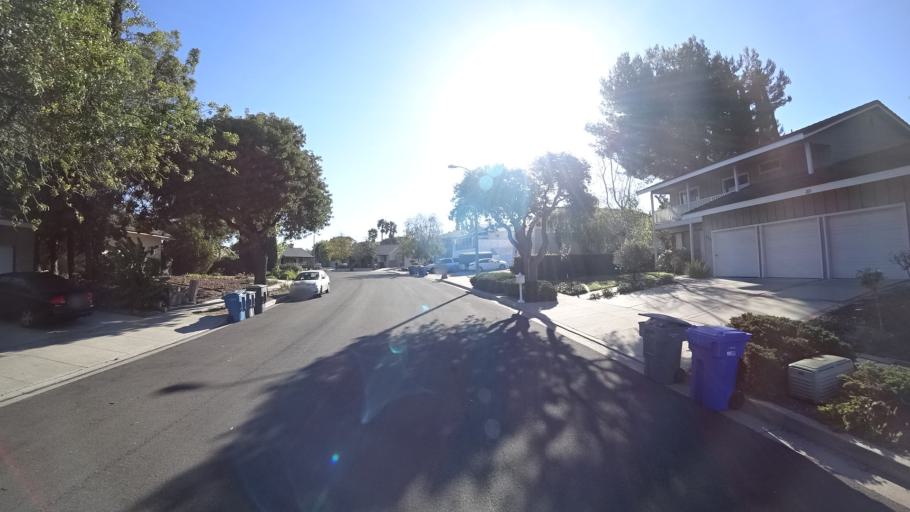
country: US
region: California
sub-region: Ventura County
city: Casa Conejo
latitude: 34.2168
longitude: -118.8963
